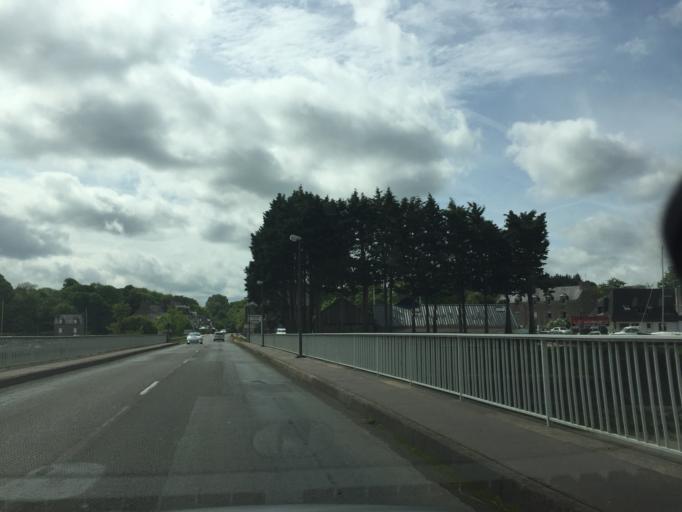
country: FR
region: Brittany
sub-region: Departement des Cotes-d'Armor
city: Crehen
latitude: 48.5736
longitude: -2.2138
